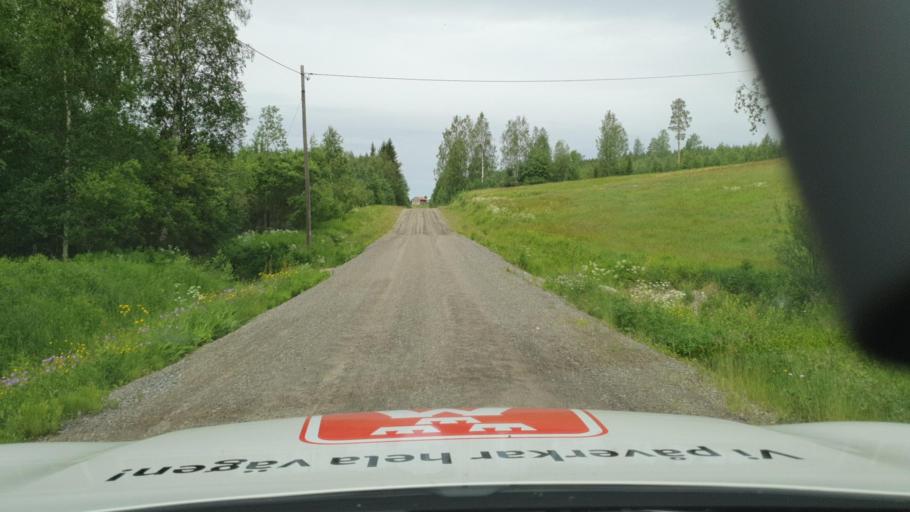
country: SE
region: Vaesterbotten
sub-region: Robertsfors Kommun
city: Robertsfors
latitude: 64.2766
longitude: 20.6903
